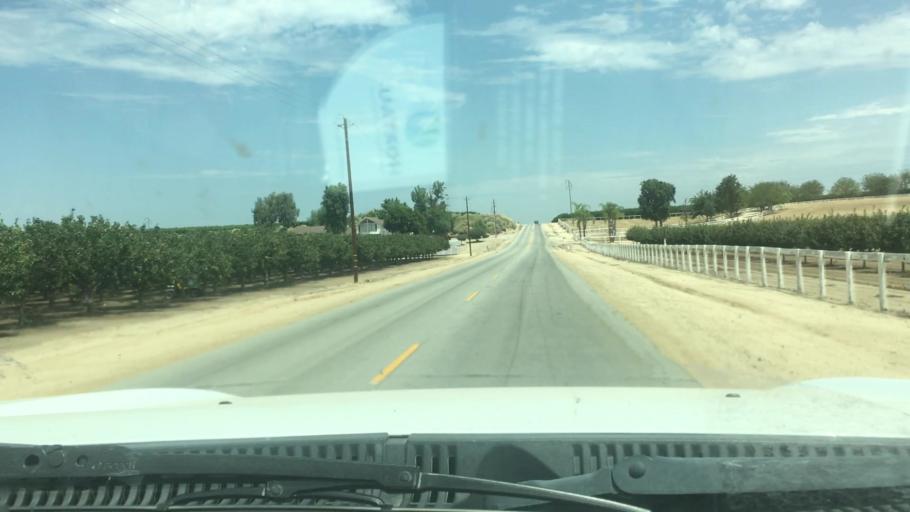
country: US
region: California
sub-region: Kern County
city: Shafter
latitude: 35.5636
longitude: -119.1511
